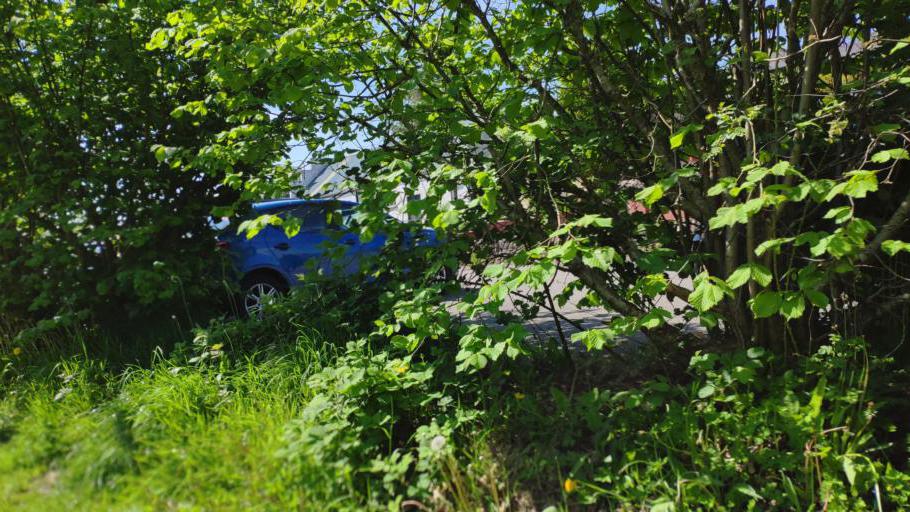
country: IE
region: Munster
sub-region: County Cork
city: Blarney
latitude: 51.9366
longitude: -8.5627
